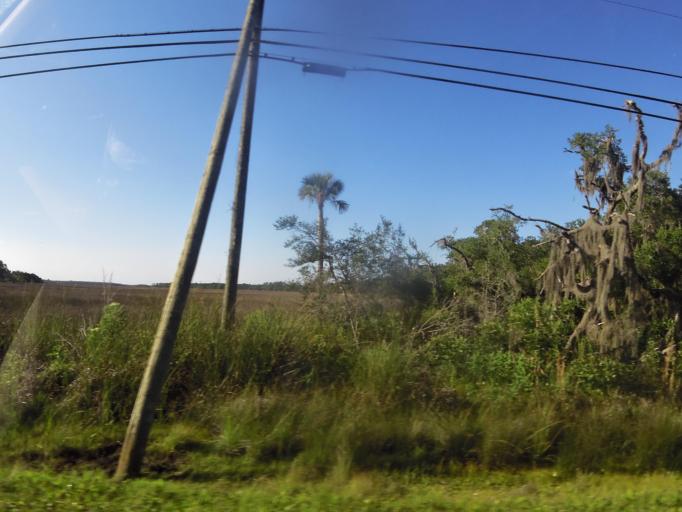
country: US
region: Florida
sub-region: Duval County
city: Atlantic Beach
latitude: 30.4603
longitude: -81.4760
